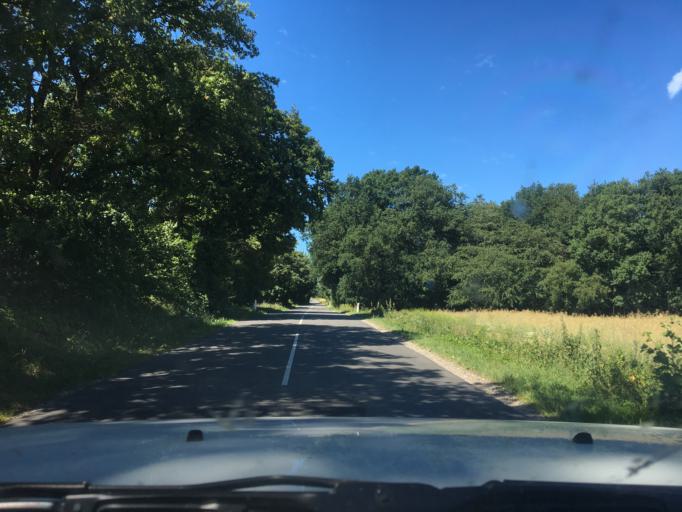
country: DK
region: Central Jutland
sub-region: Syddjurs Kommune
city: Hornslet
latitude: 56.3270
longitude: 10.3587
